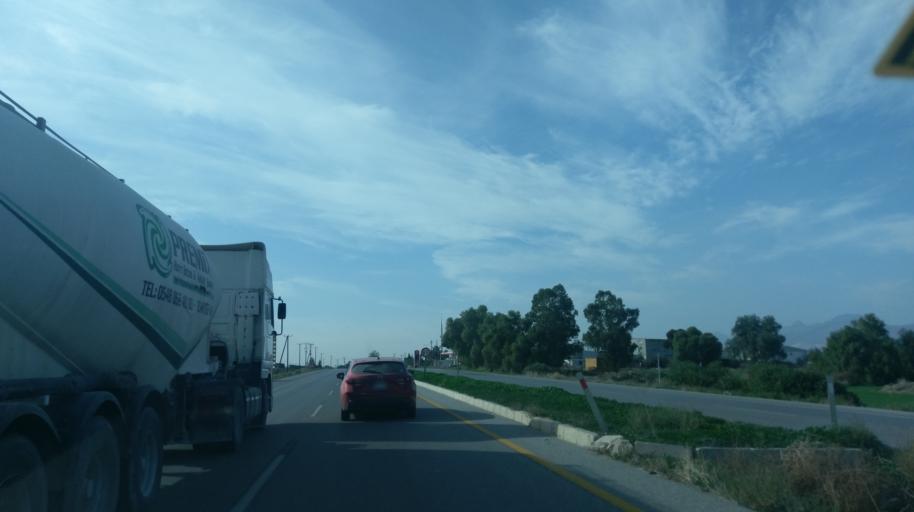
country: CY
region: Larnaka
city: Athienou
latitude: 35.2117
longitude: 33.5308
